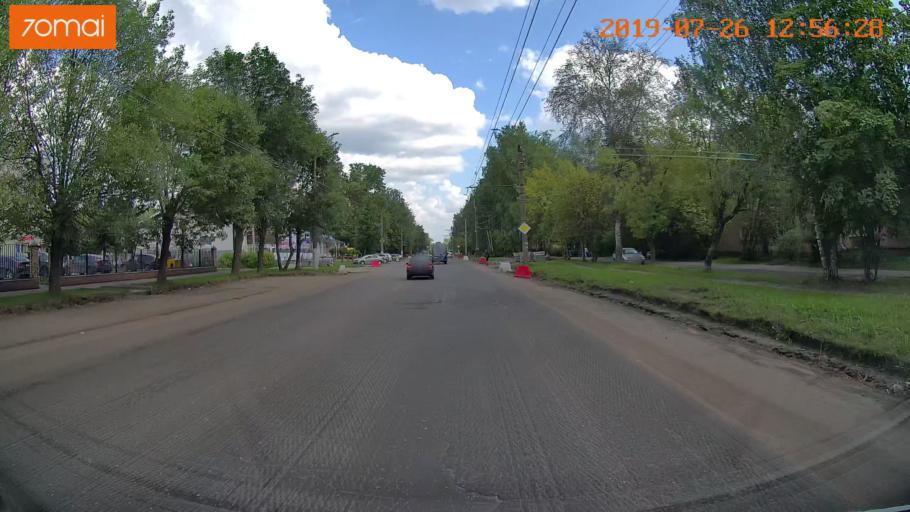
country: RU
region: Ivanovo
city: Bogorodskoye
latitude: 57.0167
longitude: 41.0117
